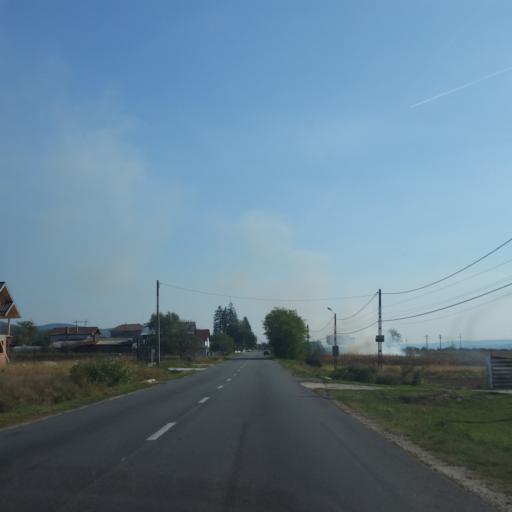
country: RO
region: Arges
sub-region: Comuna Baiculesti
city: Baiculesti
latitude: 45.0848
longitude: 24.6792
